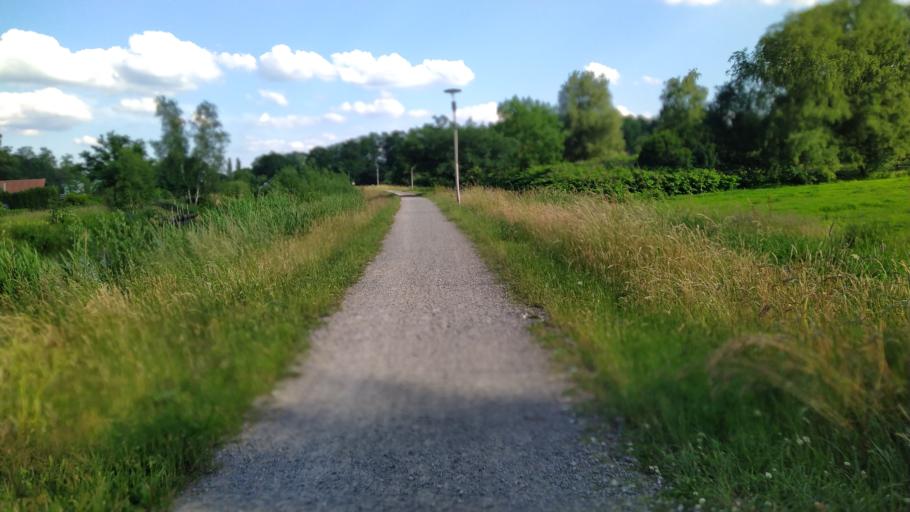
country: DE
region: Lower Saxony
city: Lintig
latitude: 53.6233
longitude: 8.8473
